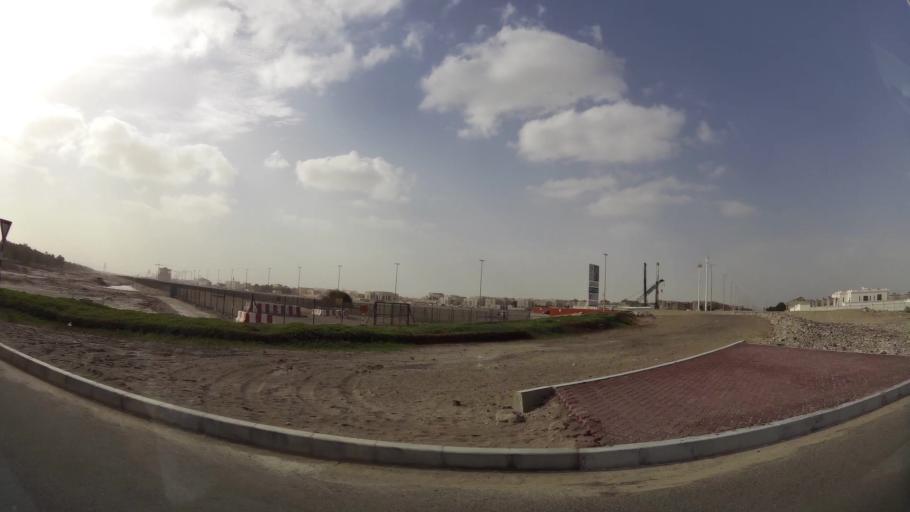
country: AE
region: Abu Dhabi
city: Abu Dhabi
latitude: 24.3981
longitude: 54.5712
